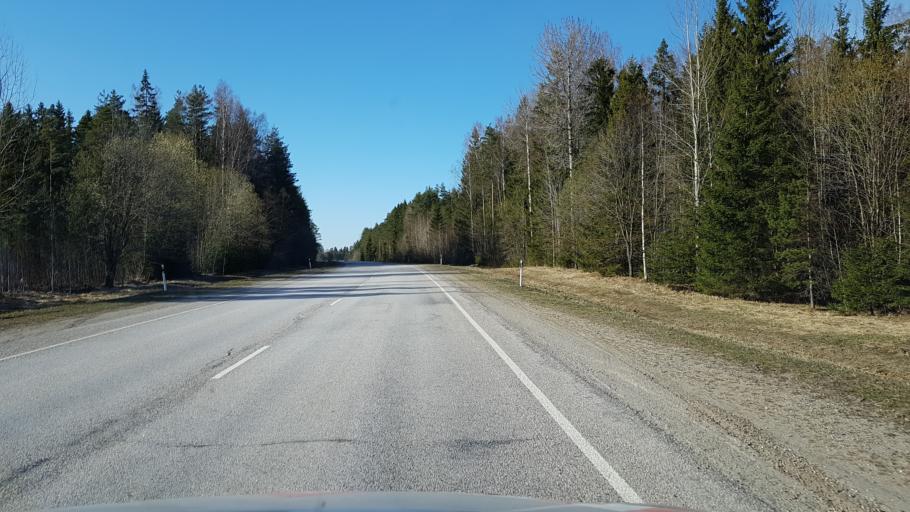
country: EE
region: Ida-Virumaa
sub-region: Johvi vald
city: Johvi
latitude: 59.1530
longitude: 27.3589
